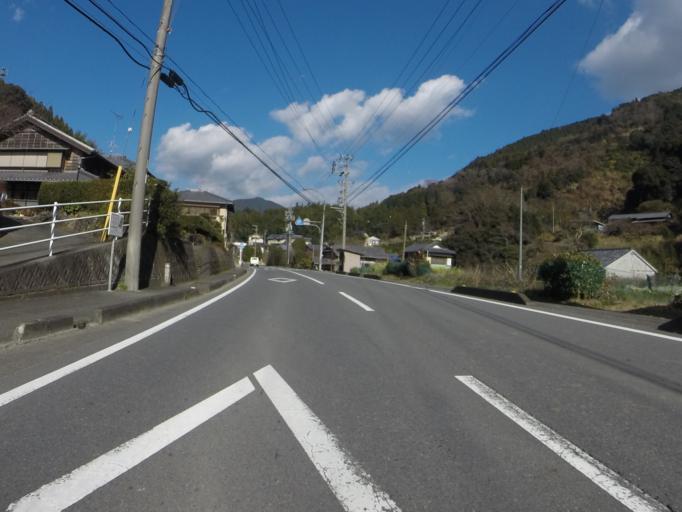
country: JP
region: Shizuoka
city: Fujinomiya
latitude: 35.1150
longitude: 138.5128
